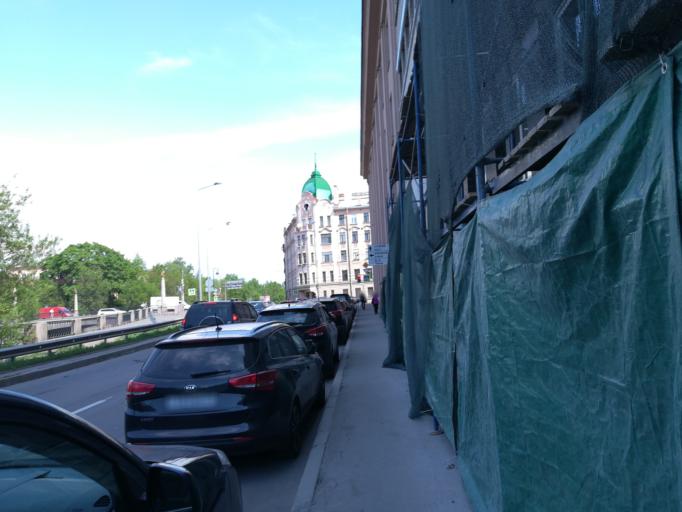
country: RU
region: St.-Petersburg
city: Vasyl'evsky Ostrov
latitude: 59.9481
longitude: 30.2674
